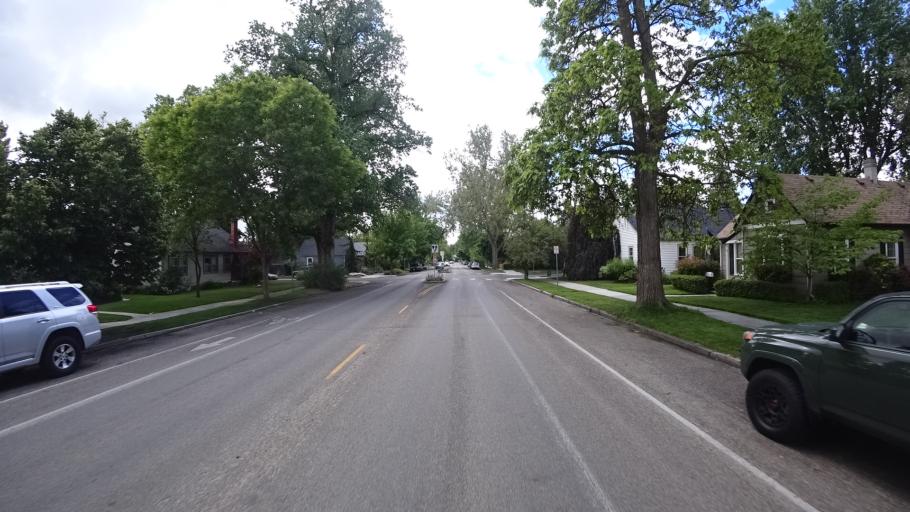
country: US
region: Idaho
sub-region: Ada County
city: Boise
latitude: 43.6298
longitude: -116.2059
